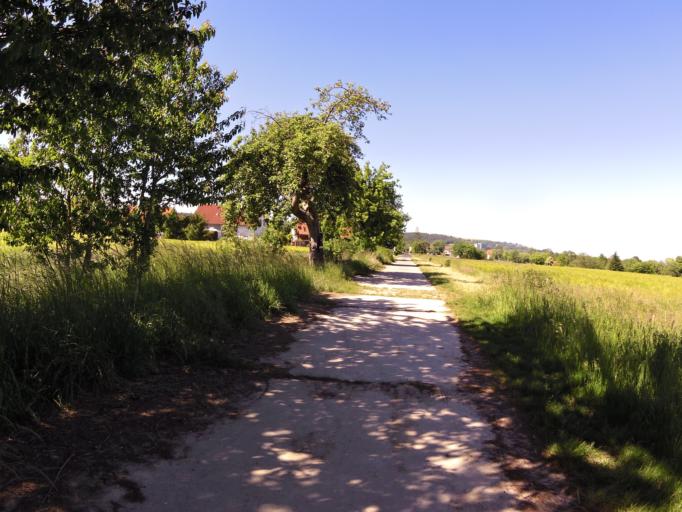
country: DE
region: Thuringia
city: Dippach
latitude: 50.9425
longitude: 10.0411
